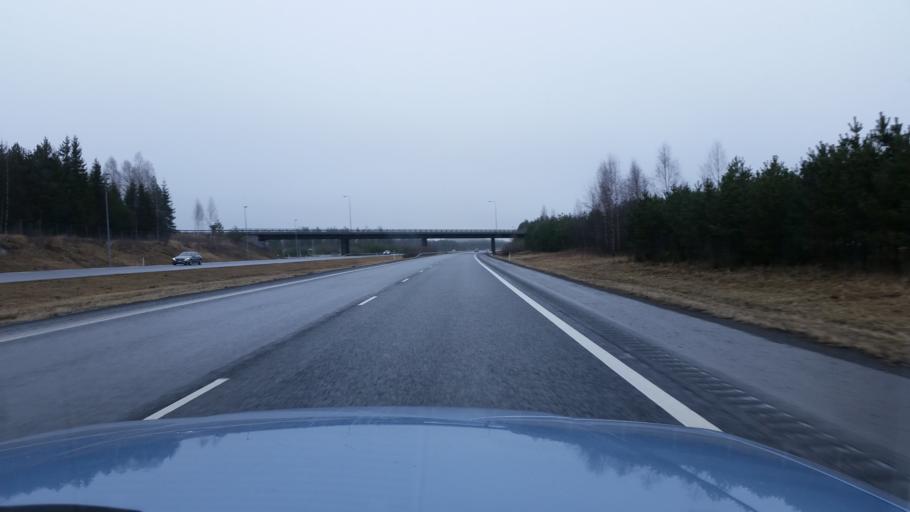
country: FI
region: Haeme
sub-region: Haemeenlinna
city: Kalvola
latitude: 61.1404
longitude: 24.0621
